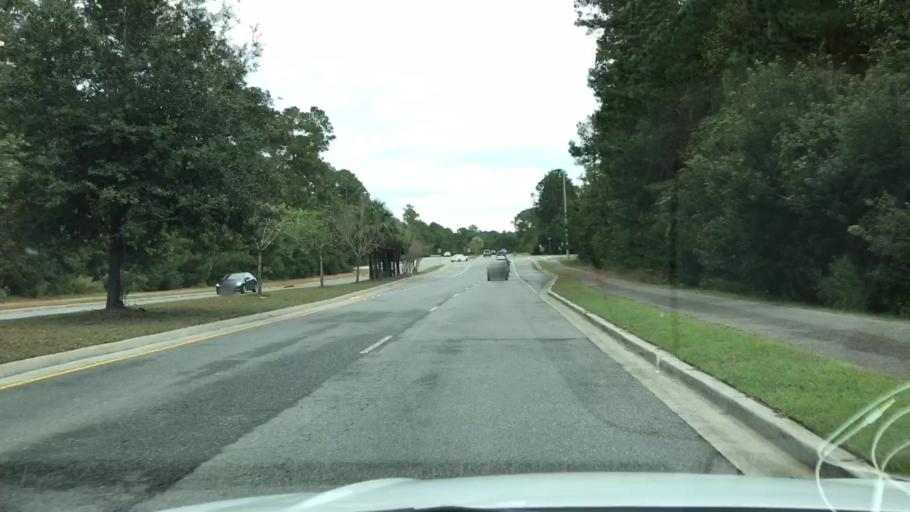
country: US
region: South Carolina
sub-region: Beaufort County
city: Bluffton
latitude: 32.2583
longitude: -80.8973
